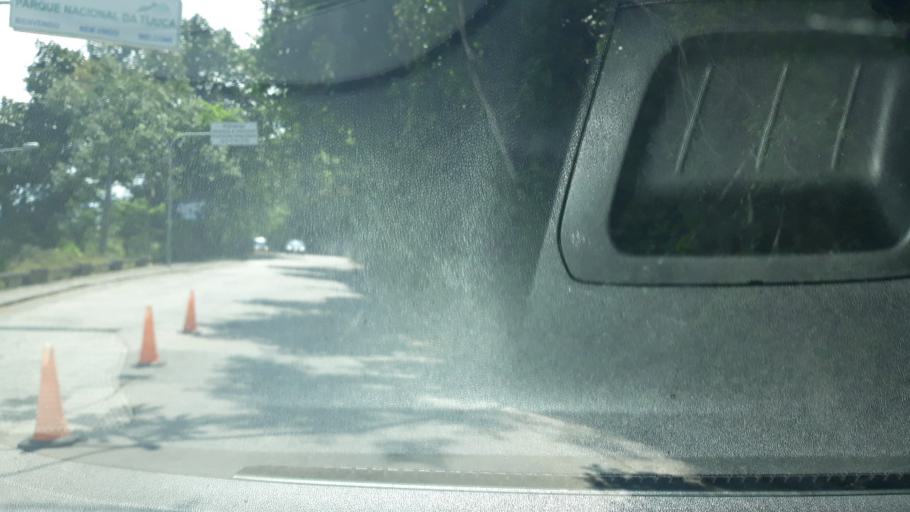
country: BR
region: Rio de Janeiro
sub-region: Rio De Janeiro
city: Rio de Janeiro
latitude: -22.9458
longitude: -43.2074
